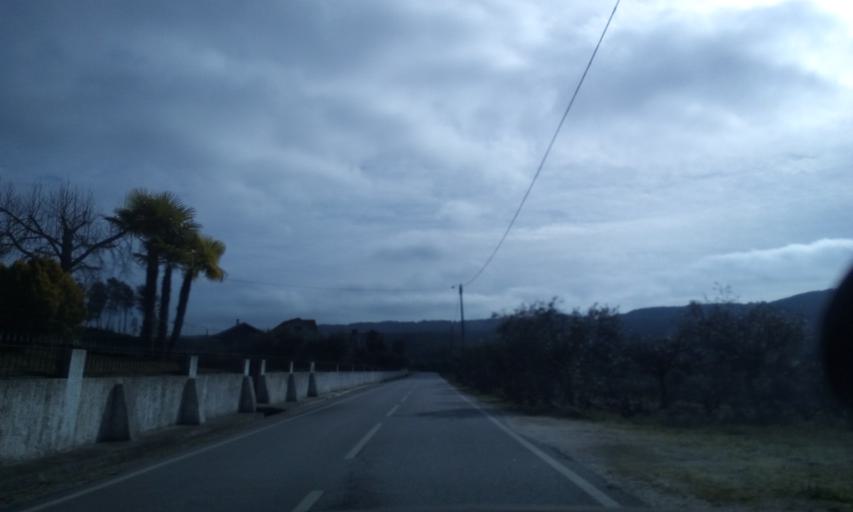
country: PT
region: Guarda
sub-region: Fornos de Algodres
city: Fornos de Algodres
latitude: 40.7037
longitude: -7.5623
